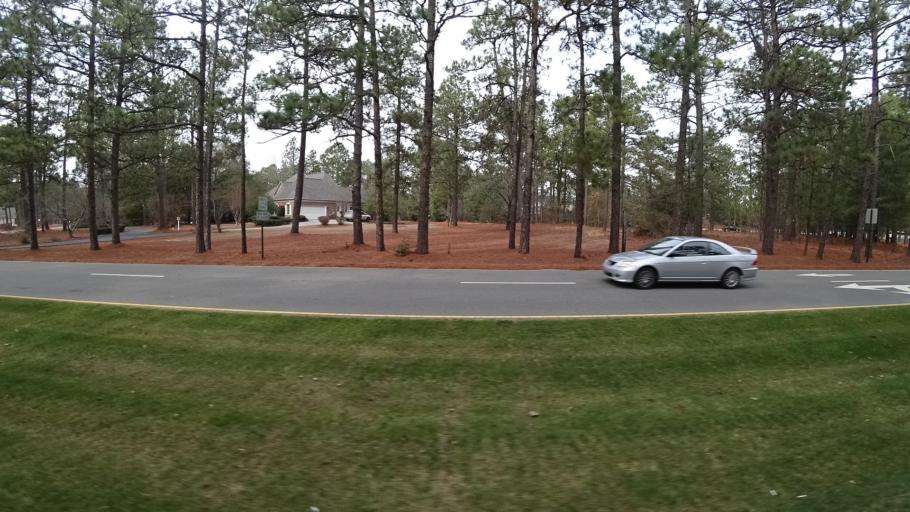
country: US
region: North Carolina
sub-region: Moore County
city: Pinehurst
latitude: 35.2008
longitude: -79.4528
